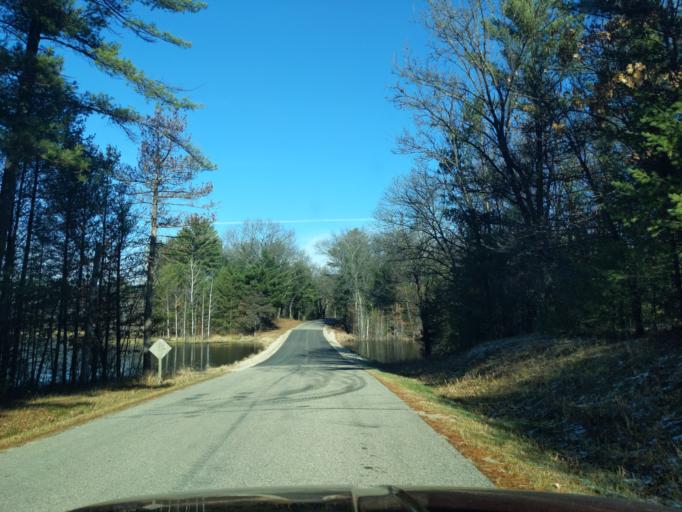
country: US
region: Wisconsin
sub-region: Waushara County
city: Silver Lake
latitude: 44.0841
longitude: -89.1938
